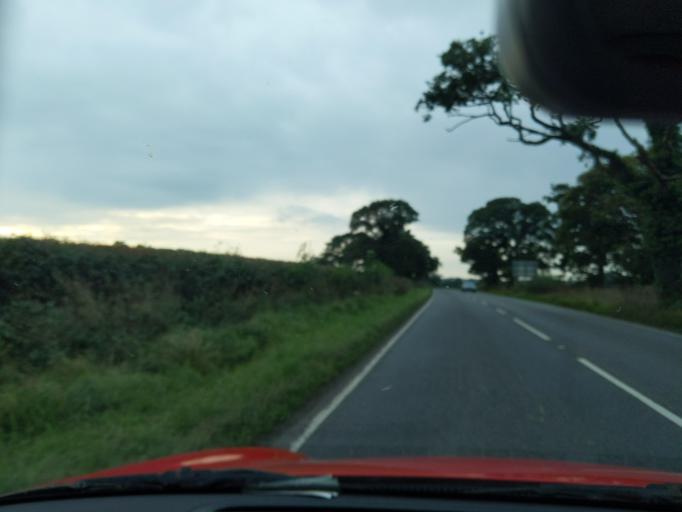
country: GB
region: England
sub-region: Devon
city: Okehampton
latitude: 50.8108
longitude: -4.0589
